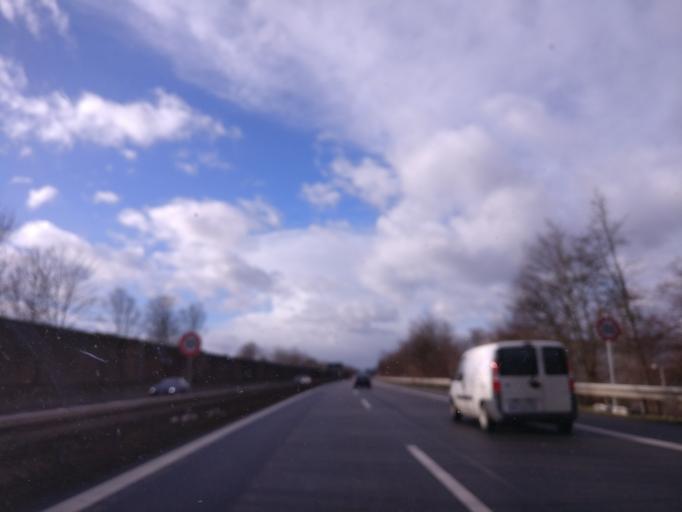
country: DE
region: Baden-Wuerttemberg
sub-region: Regierungsbezirk Stuttgart
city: Weinstadt-Endersbach
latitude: 48.8148
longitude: 9.3745
